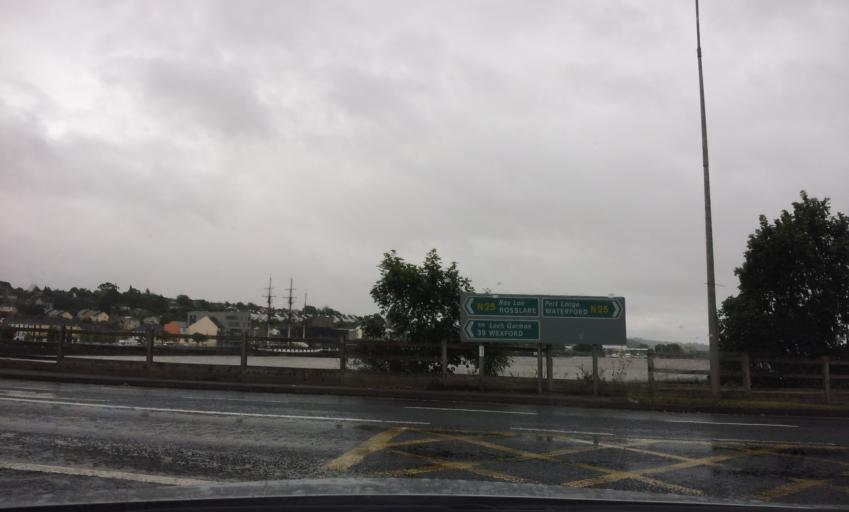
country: IE
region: Leinster
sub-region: Loch Garman
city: New Ross
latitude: 52.3968
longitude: -6.9485
